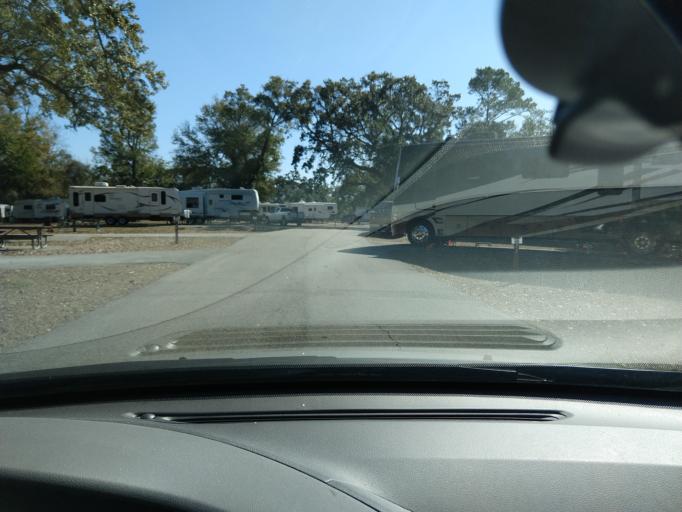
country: US
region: Mississippi
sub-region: Jackson County
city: Ocean Springs
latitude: 30.3970
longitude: -88.7961
